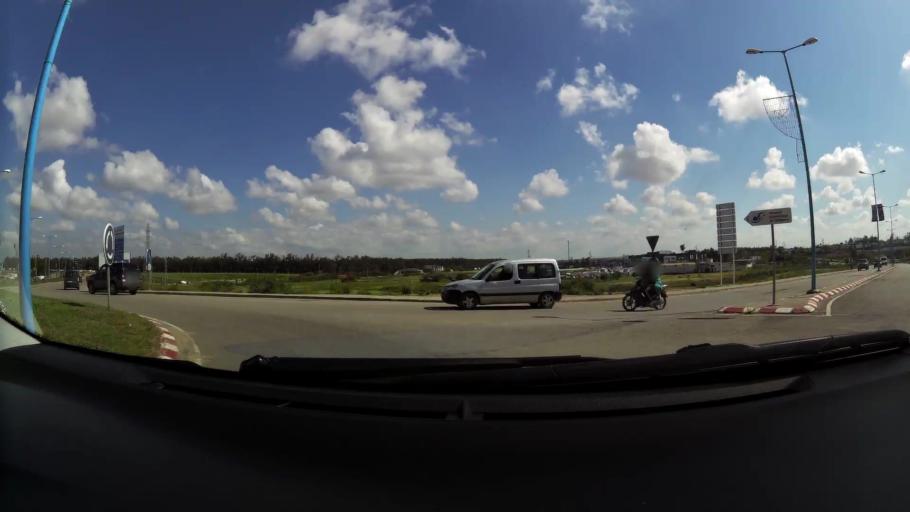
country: MA
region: Grand Casablanca
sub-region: Nouaceur
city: Bouskoura
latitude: 33.4845
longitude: -7.6358
